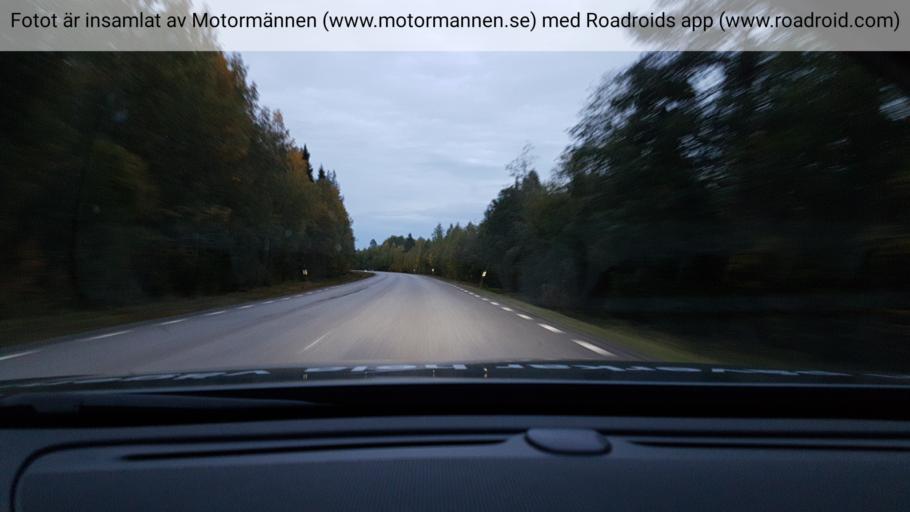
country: SE
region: Norrbotten
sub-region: Alvsbyns Kommun
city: AElvsbyn
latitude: 65.7824
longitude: 20.7674
